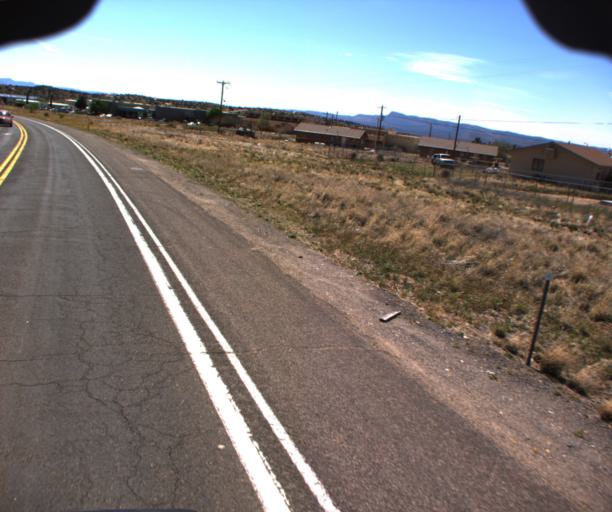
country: US
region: Arizona
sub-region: Mohave County
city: Peach Springs
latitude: 35.5397
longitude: -113.4165
